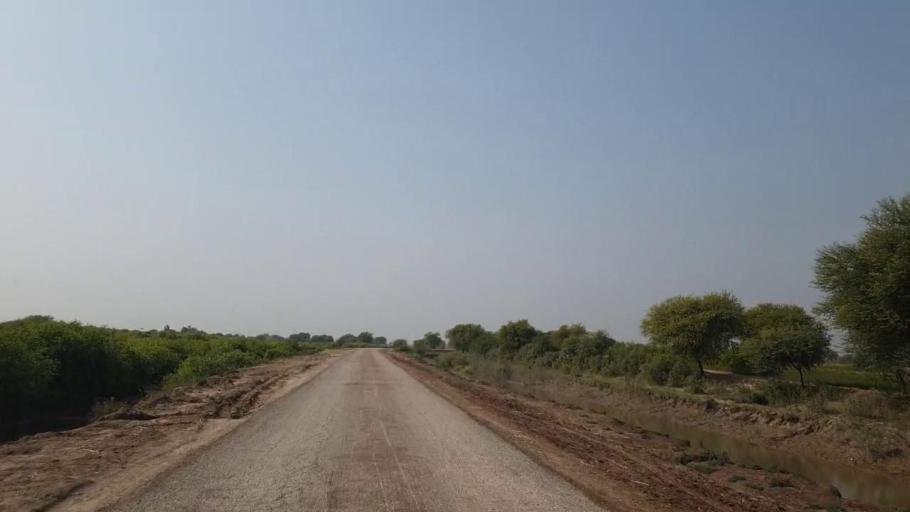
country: PK
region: Sindh
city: Kario
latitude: 24.9471
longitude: 68.5310
